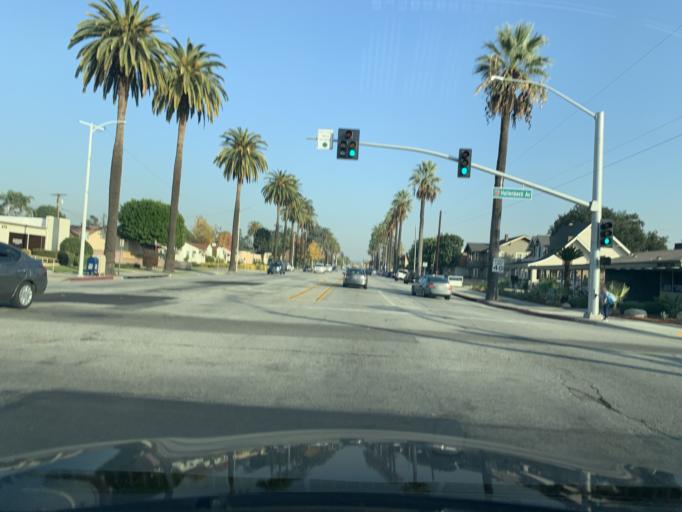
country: US
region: California
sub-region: Los Angeles County
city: Covina
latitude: 34.0863
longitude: -117.8991
